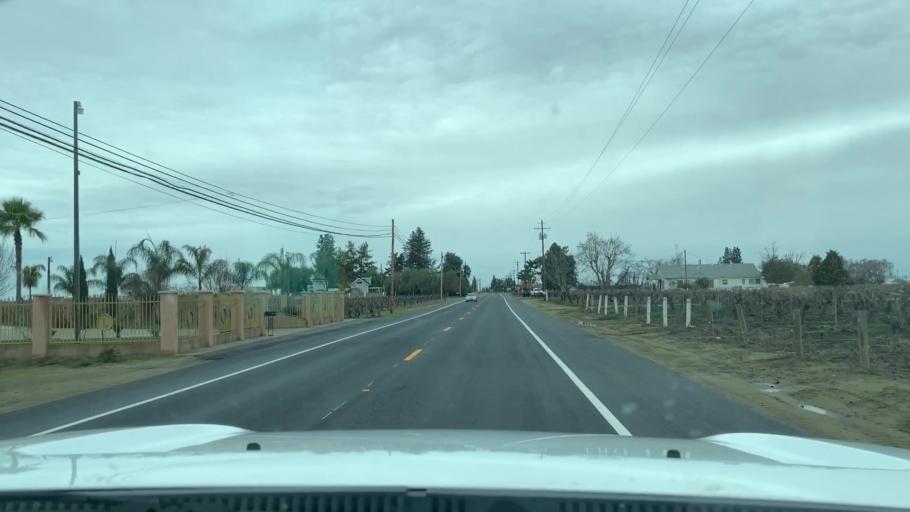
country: US
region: California
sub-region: Fresno County
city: Selma
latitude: 36.5575
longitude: -119.6825
